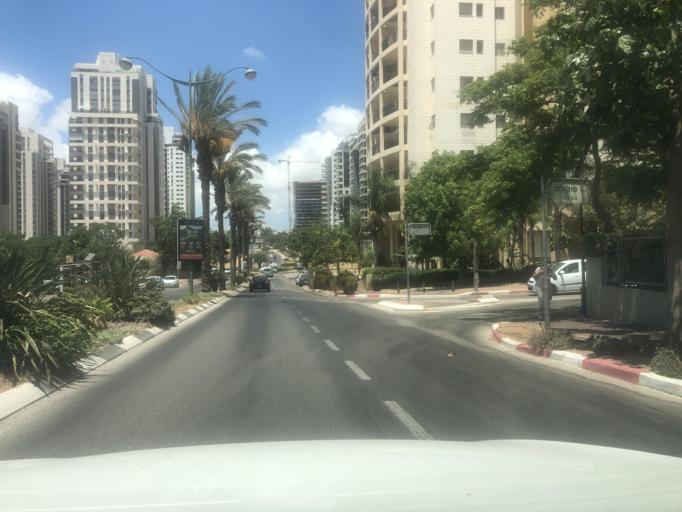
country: IL
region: Central District
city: Hod HaSharon
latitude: 32.1630
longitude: 34.9024
